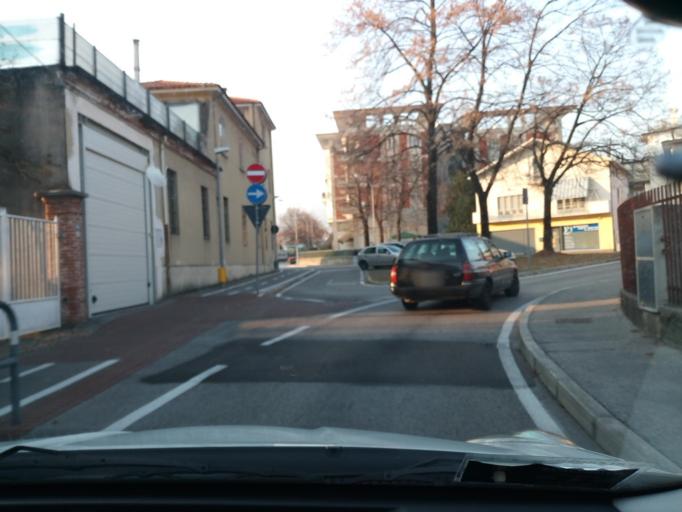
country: IT
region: Veneto
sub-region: Provincia di Vicenza
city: Schio
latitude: 45.7128
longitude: 11.3707
